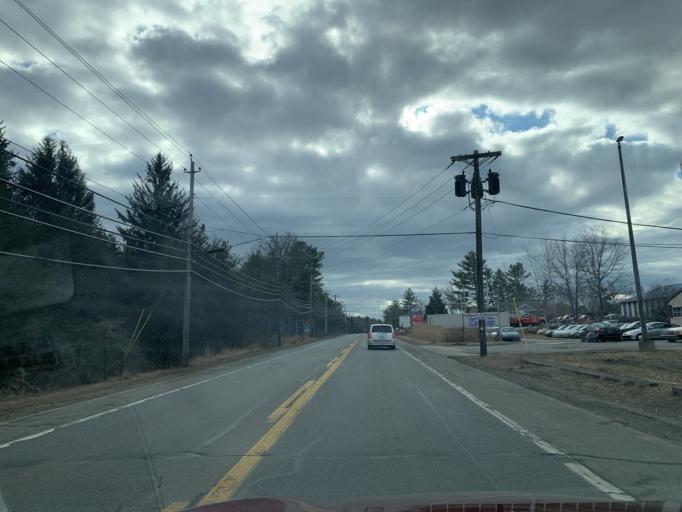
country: US
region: Massachusetts
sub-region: Essex County
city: Newburyport
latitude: 42.7864
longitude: -70.8799
